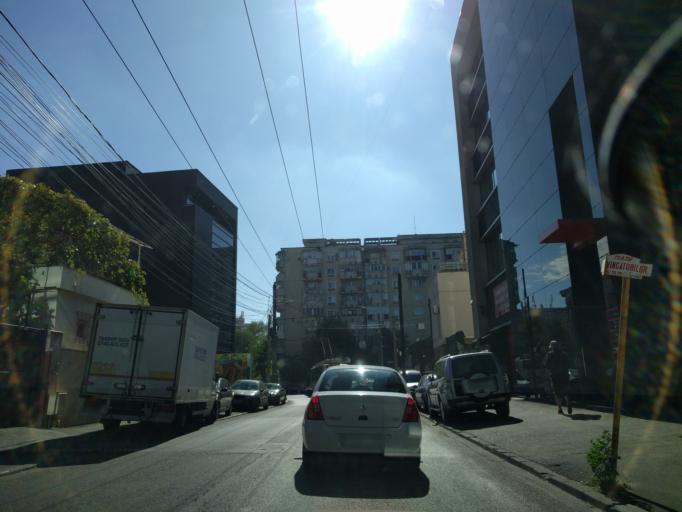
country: RO
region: Bucuresti
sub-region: Municipiul Bucuresti
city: Bucharest
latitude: 44.4295
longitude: 26.1308
